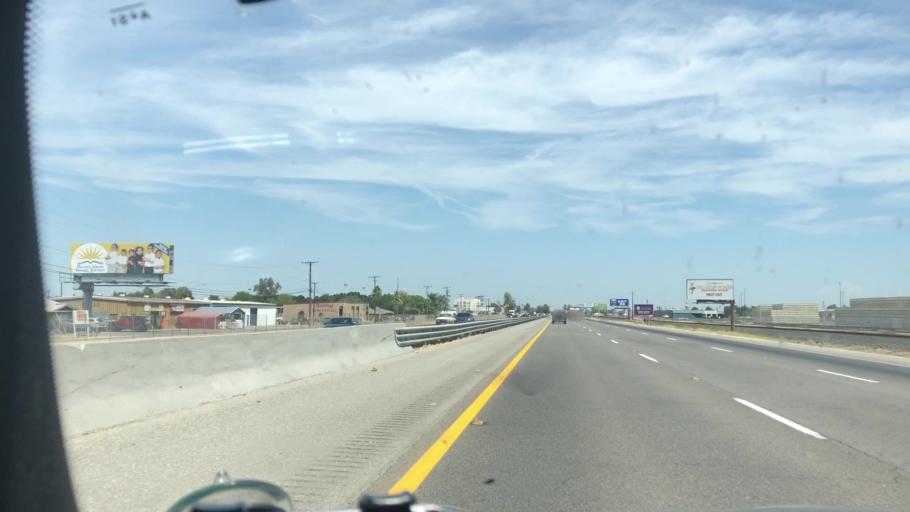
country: US
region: California
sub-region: Kern County
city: Delano
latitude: 35.7364
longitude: -119.2407
